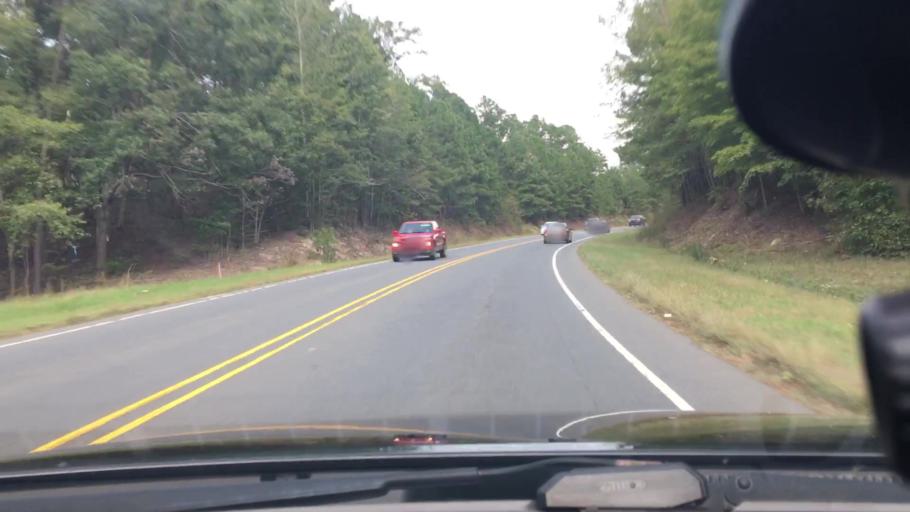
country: US
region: North Carolina
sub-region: Montgomery County
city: Mount Gilead
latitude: 35.3125
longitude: -80.0520
